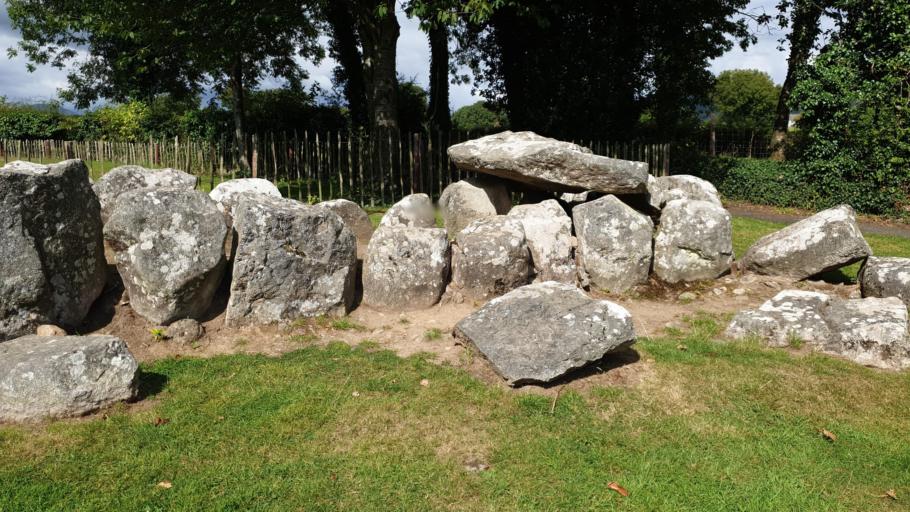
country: IE
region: Leinster
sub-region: Lu
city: Blackrock
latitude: 54.0368
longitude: -6.3472
